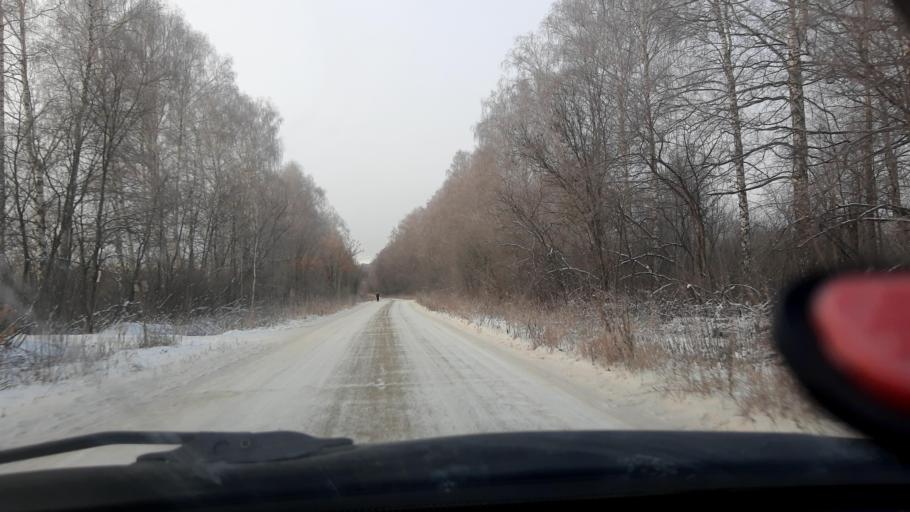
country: RU
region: Bashkortostan
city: Iglino
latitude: 54.8425
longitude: 56.4606
